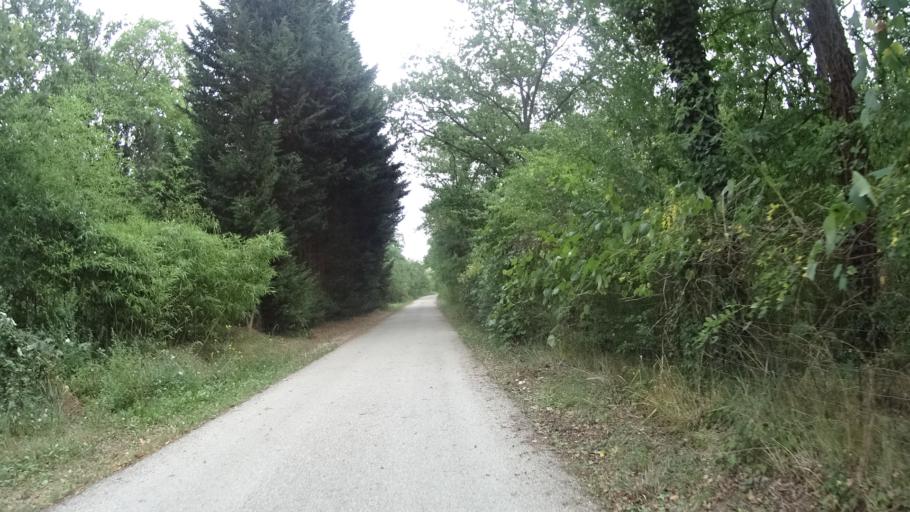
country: FR
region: Centre
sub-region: Departement du Loiret
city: Clery-Saint-Andre
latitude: 47.8394
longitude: 1.7295
